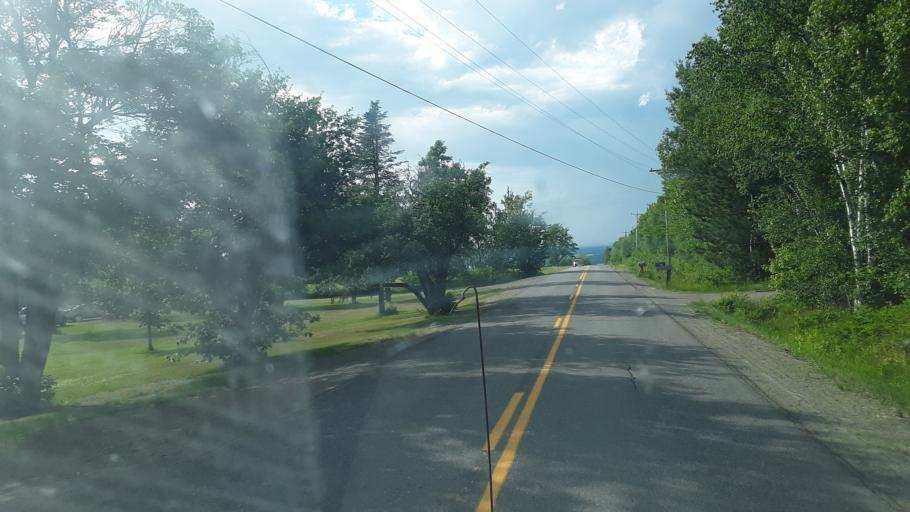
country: US
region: Maine
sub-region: Washington County
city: Calais
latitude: 45.0924
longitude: -67.5060
